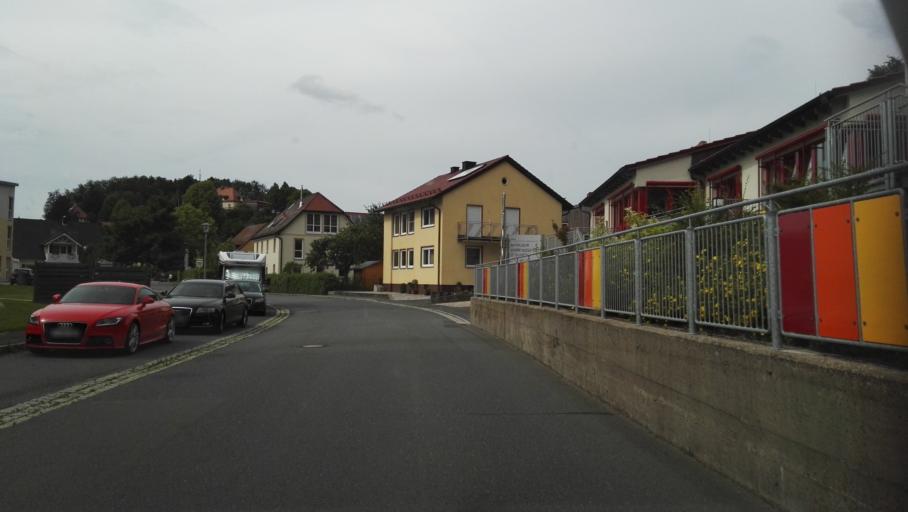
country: DE
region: Bavaria
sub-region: Upper Franconia
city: Waischenfeld
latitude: 49.8425
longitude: 11.3489
